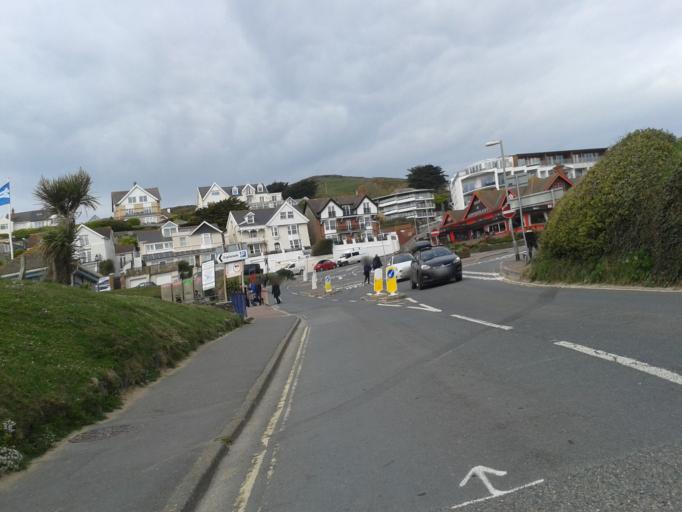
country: GB
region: England
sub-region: Devon
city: Braunton
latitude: 51.1720
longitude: -4.2079
